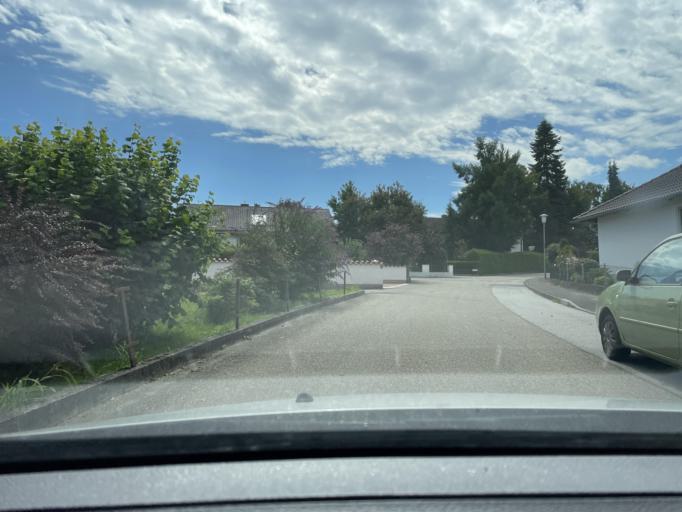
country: DE
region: Bavaria
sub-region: Lower Bavaria
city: Altfraunhofen
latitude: 48.4482
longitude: 12.1783
